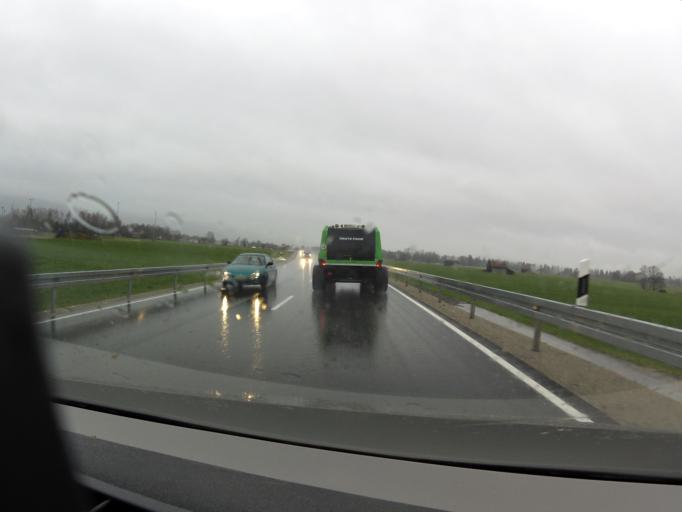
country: DE
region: Bavaria
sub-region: Upper Bavaria
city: Bichl
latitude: 47.7279
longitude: 11.4079
